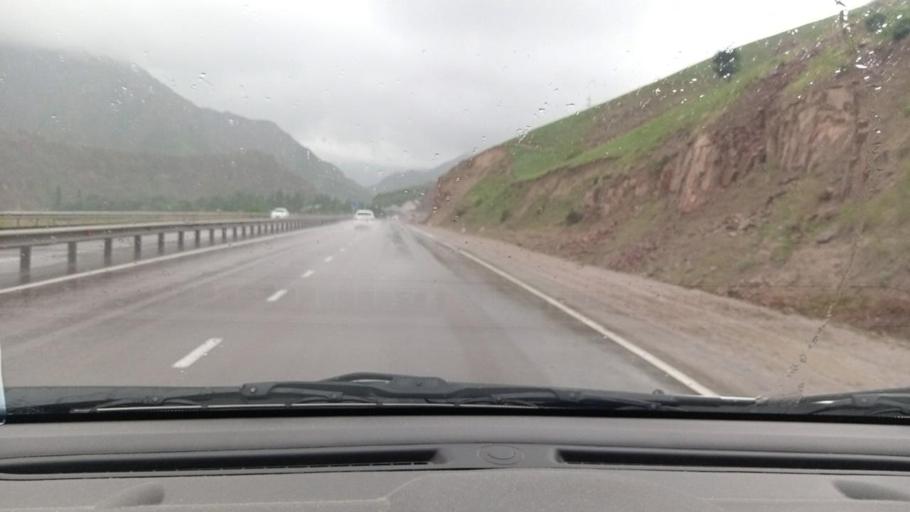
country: UZ
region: Toshkent
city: Angren
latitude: 41.1129
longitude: 70.3388
